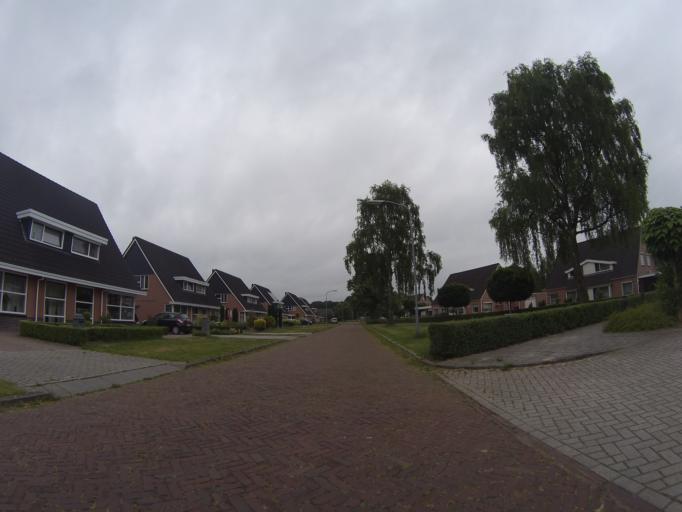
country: NL
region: Drenthe
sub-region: Gemeente Emmen
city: Emmer-Compascuum
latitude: 52.8143
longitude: 7.0558
